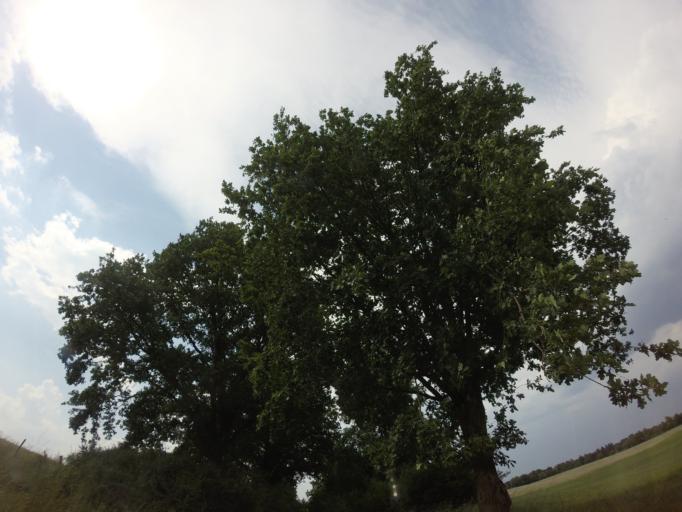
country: PL
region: West Pomeranian Voivodeship
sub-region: Powiat choszczenski
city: Krzecin
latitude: 53.1328
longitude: 15.5823
